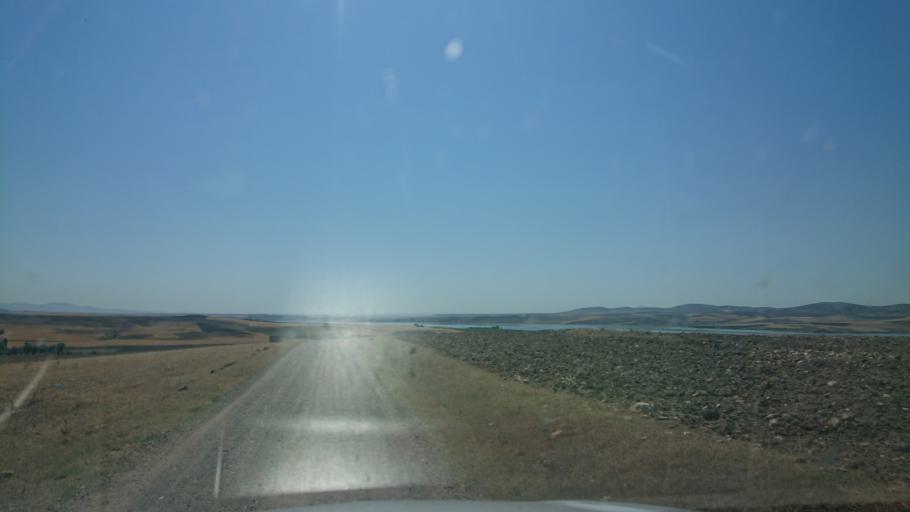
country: TR
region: Aksaray
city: Sariyahsi
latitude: 39.0562
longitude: 33.8893
